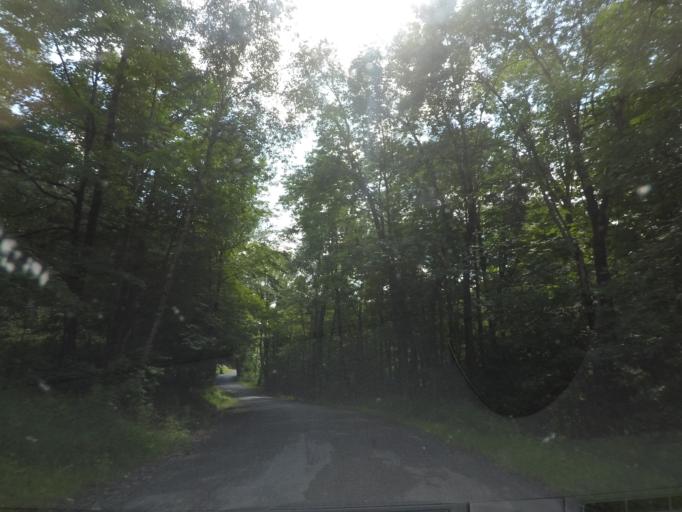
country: US
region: New York
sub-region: Rensselaer County
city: Averill Park
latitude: 42.5867
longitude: -73.5189
